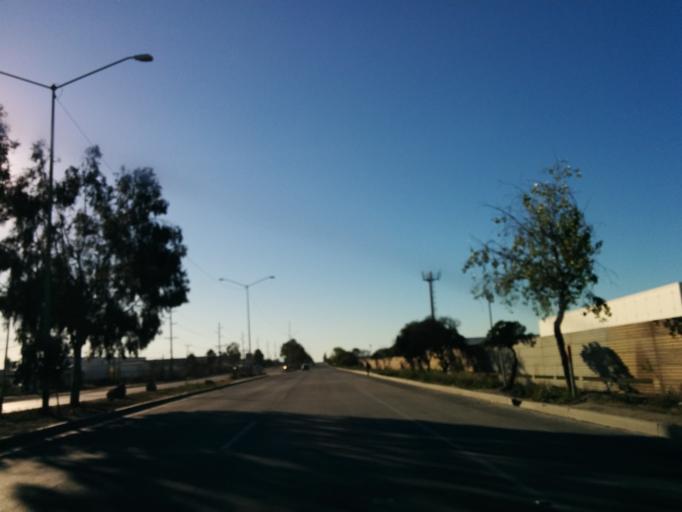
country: MX
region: Baja California
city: Tijuana
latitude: 32.5487
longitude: -116.9548
